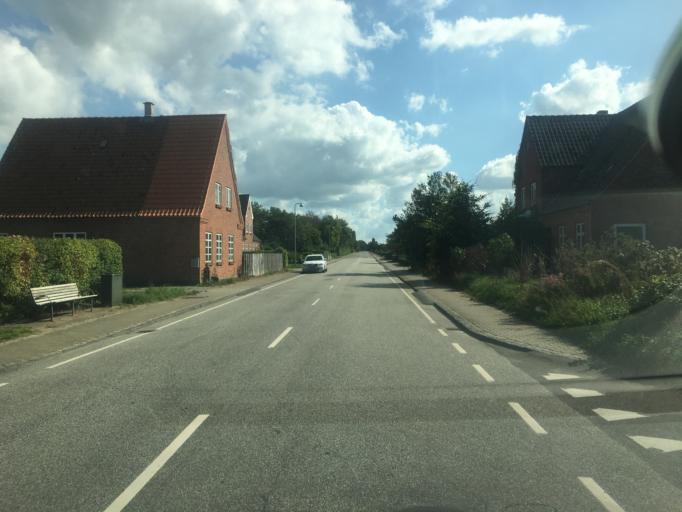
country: DE
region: Schleswig-Holstein
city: Ellhoft
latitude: 54.9405
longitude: 8.9685
